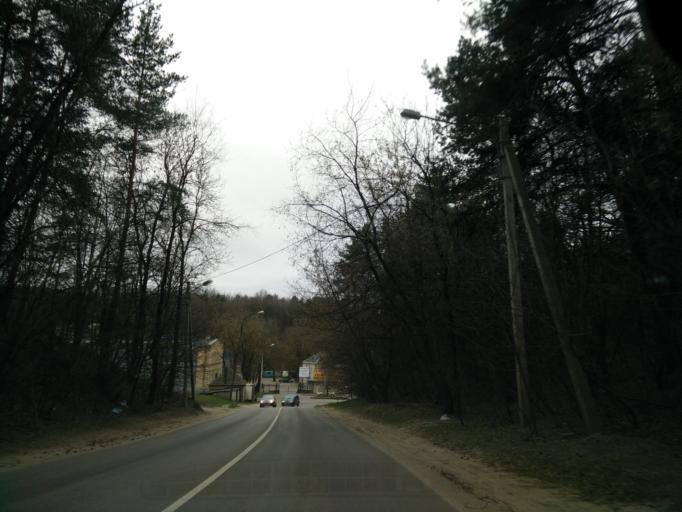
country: LT
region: Vilnius County
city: Vilkpede
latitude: 54.6644
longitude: 25.2436
